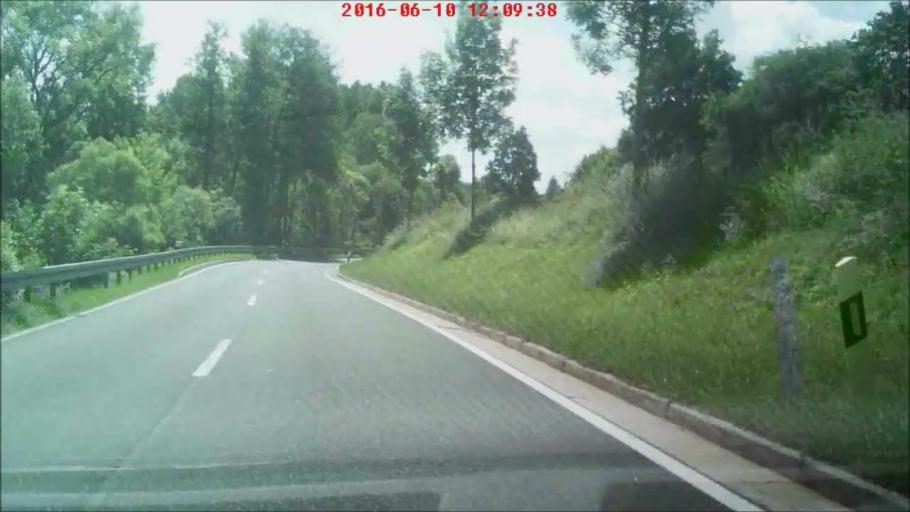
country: DE
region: Thuringia
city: Ellingshausen
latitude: 50.5517
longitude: 10.4743
